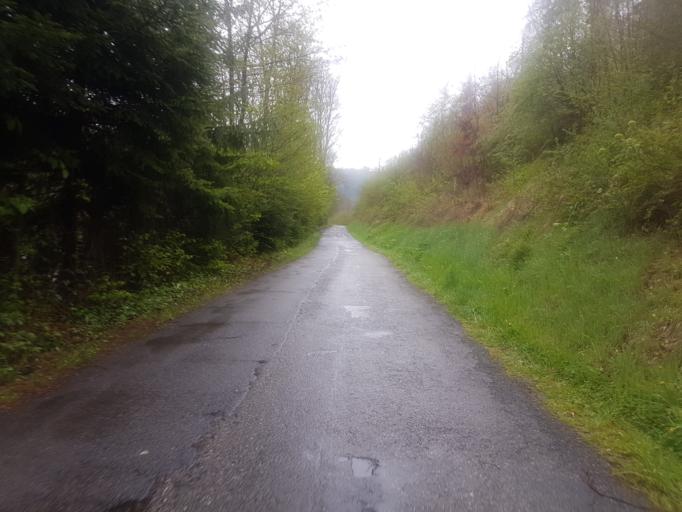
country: DE
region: Baden-Wuerttemberg
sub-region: Freiburg Region
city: Villingendorf
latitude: 48.2118
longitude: 8.6098
